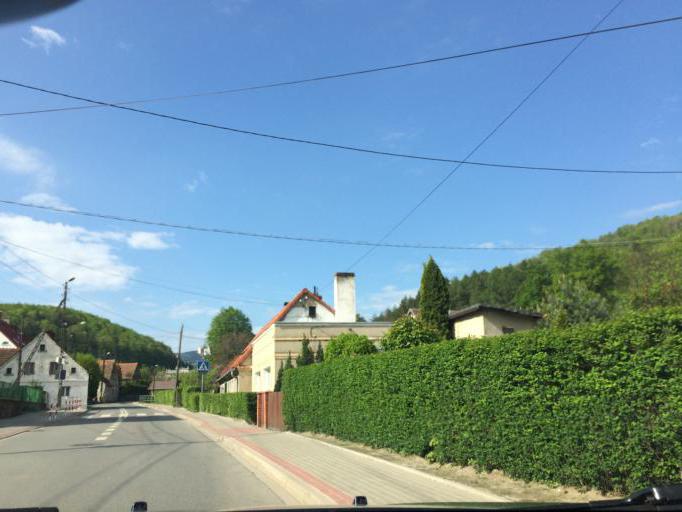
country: PL
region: Lower Silesian Voivodeship
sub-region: Powiat dzierzoniowski
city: Pieszyce
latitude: 50.6989
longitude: 16.5648
